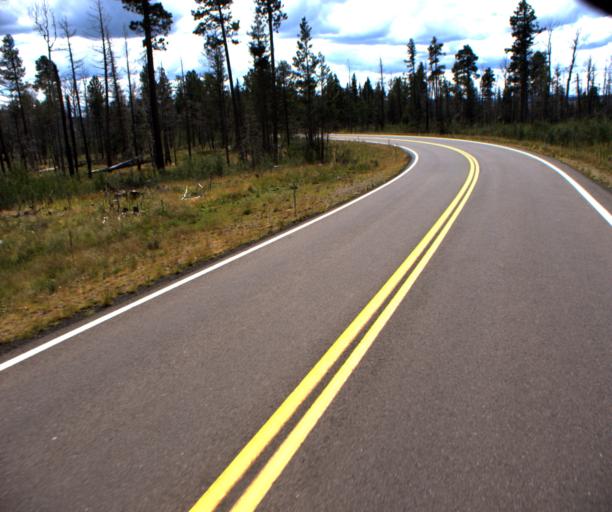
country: US
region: Arizona
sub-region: Apache County
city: Eagar
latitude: 33.9236
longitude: -109.4535
